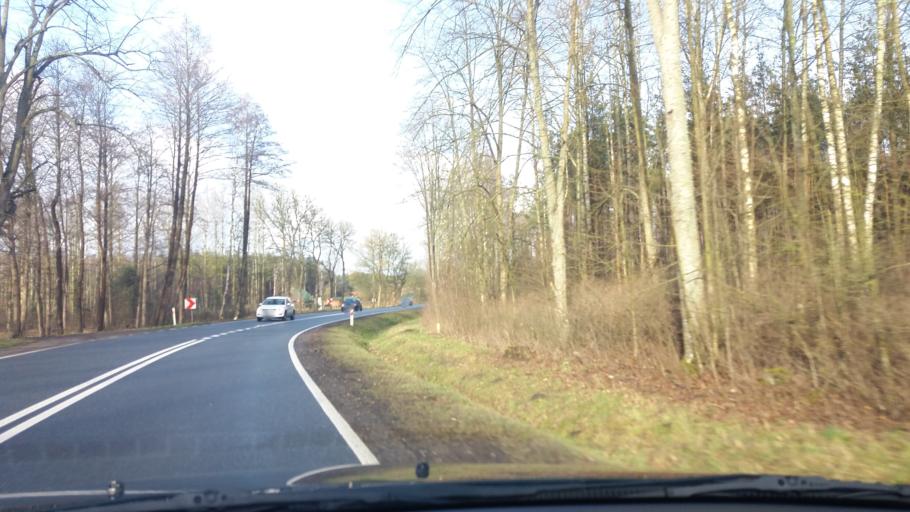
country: PL
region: Masovian Voivodeship
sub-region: Powiat przasnyski
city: Chorzele
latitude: 53.2809
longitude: 20.8987
